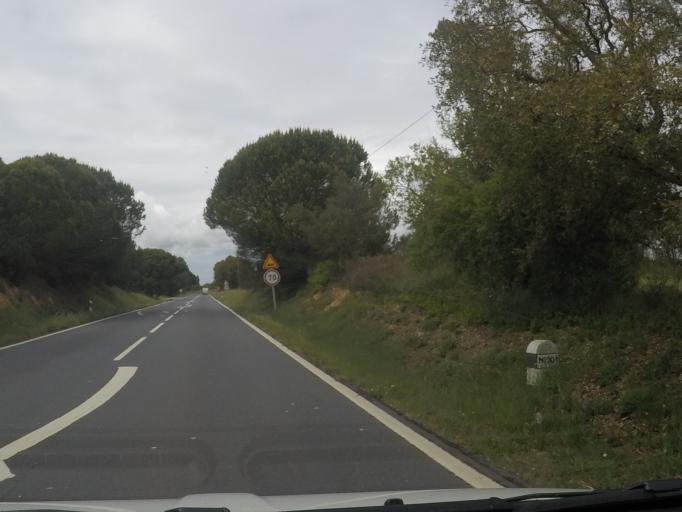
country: PT
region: Setubal
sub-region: Sines
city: Porto Covo
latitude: 37.8772
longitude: -8.7435
